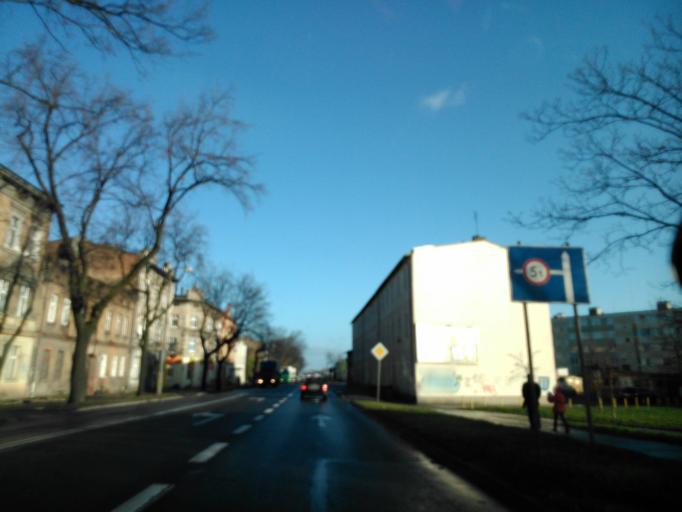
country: PL
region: Kujawsko-Pomorskie
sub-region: Powiat inowroclawski
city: Inowroclaw
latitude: 52.8024
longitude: 18.2681
